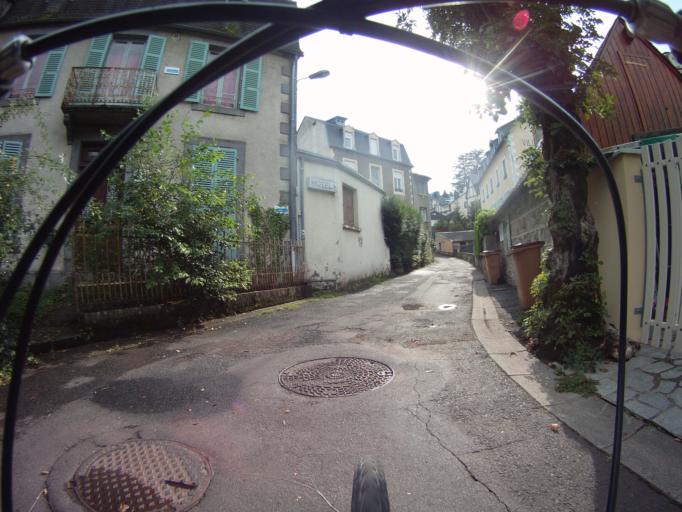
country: FR
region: Auvergne
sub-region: Departement du Puy-de-Dome
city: La Bourboule
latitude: 45.5866
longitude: 2.7382
